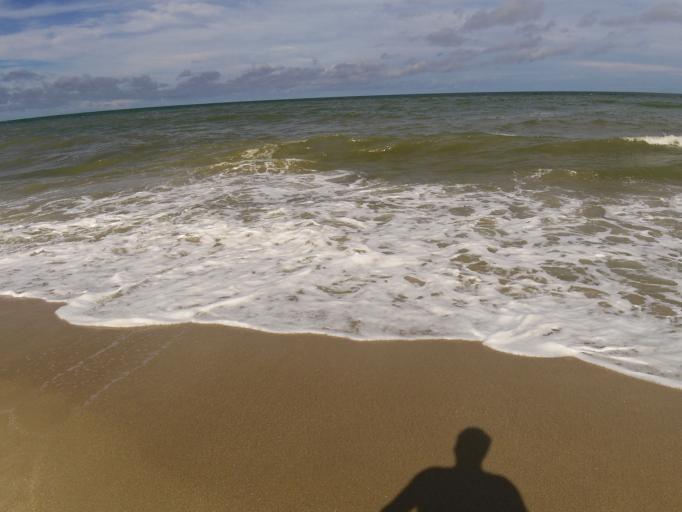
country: US
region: Florida
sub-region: Indian River County
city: Sebastian
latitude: 27.8541
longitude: -80.4440
